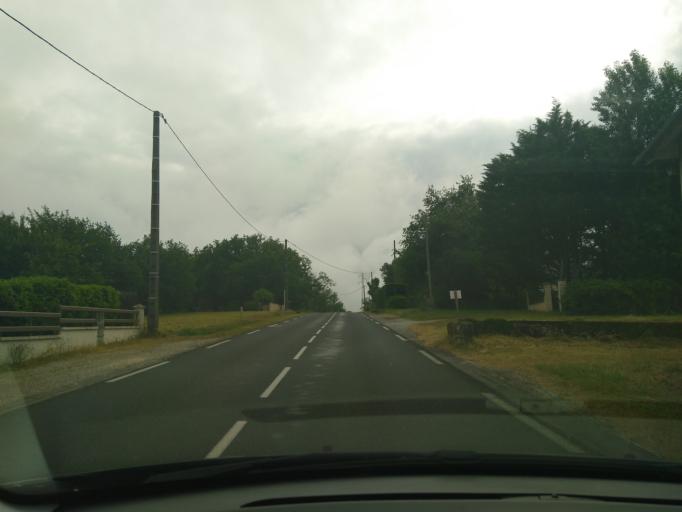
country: FR
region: Limousin
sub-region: Departement de la Correze
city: Brive-la-Gaillarde
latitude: 45.1039
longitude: 1.5386
